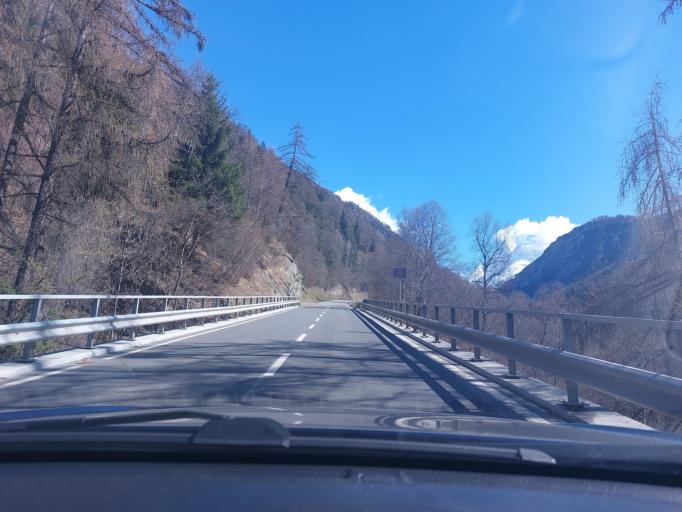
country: CH
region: Valais
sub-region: Herens District
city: Evolene
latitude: 46.1452
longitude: 7.4626
